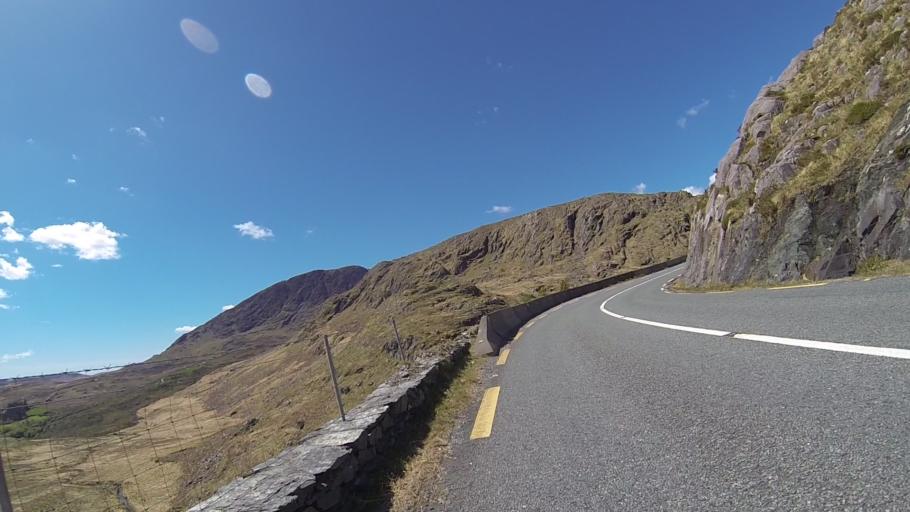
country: IE
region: Munster
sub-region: Ciarrai
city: Kenmare
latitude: 51.9333
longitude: -9.6519
